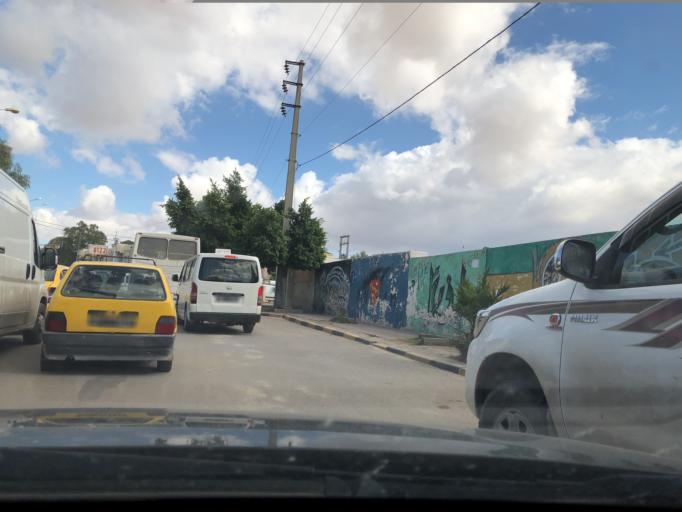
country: TN
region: Al Qasrayn
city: Kasserine
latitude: 35.1659
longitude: 8.8303
